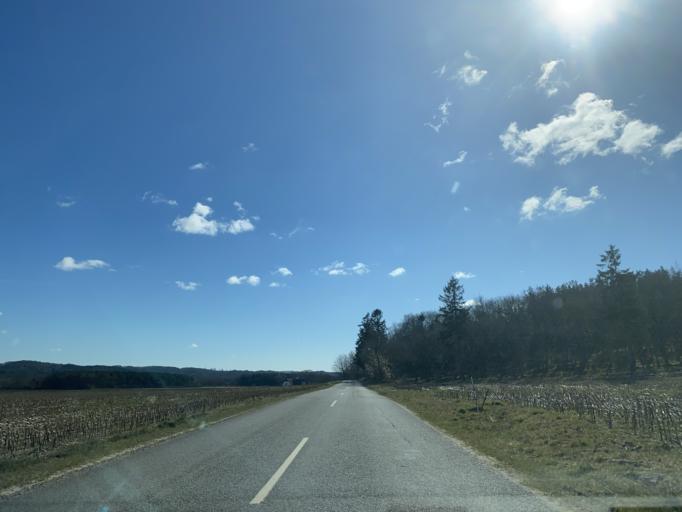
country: DK
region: Central Jutland
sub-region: Silkeborg Kommune
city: Svejbaek
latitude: 56.2466
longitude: 9.6570
